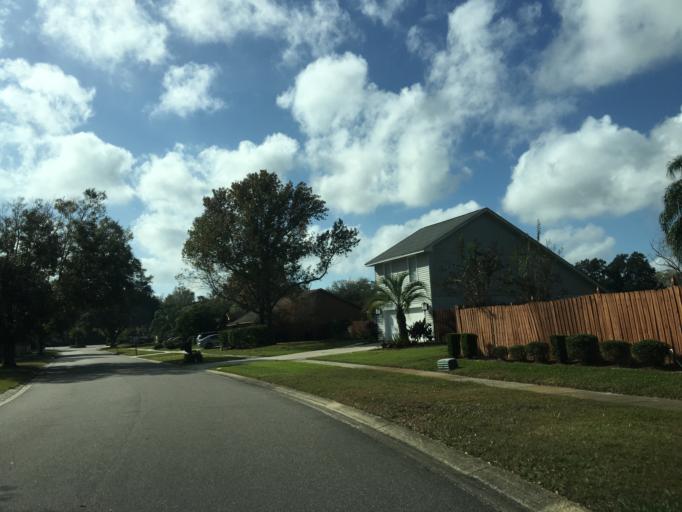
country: US
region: Florida
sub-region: Orange County
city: Azalea Park
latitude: 28.5122
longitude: -81.2761
